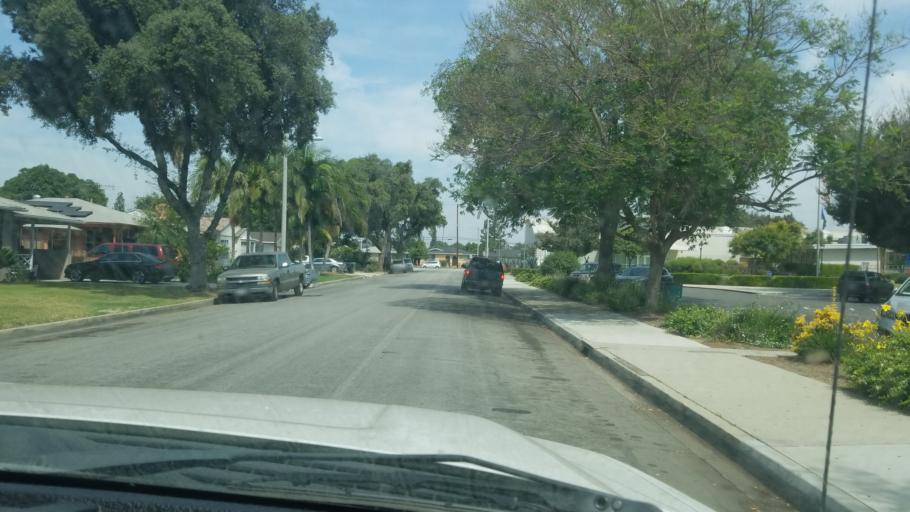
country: US
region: California
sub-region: Los Angeles County
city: West Whittier-Los Nietos
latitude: 33.9787
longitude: -118.0618
